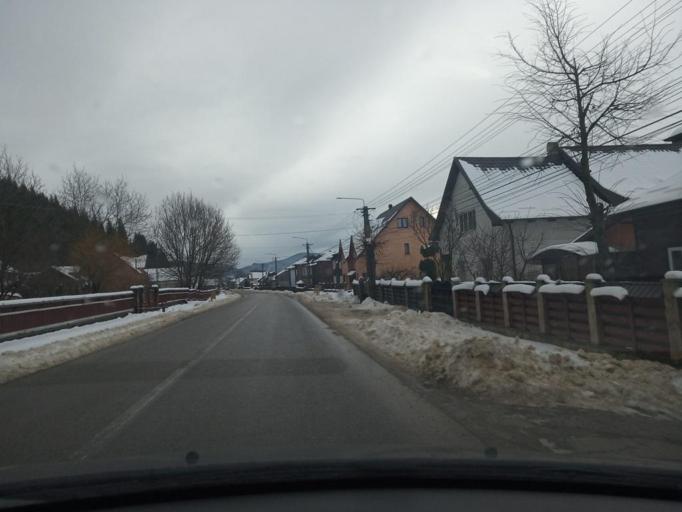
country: RO
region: Suceava
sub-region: Comuna Manastirea Humorului
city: Manastirea Humorului
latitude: 47.5887
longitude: 25.8686
